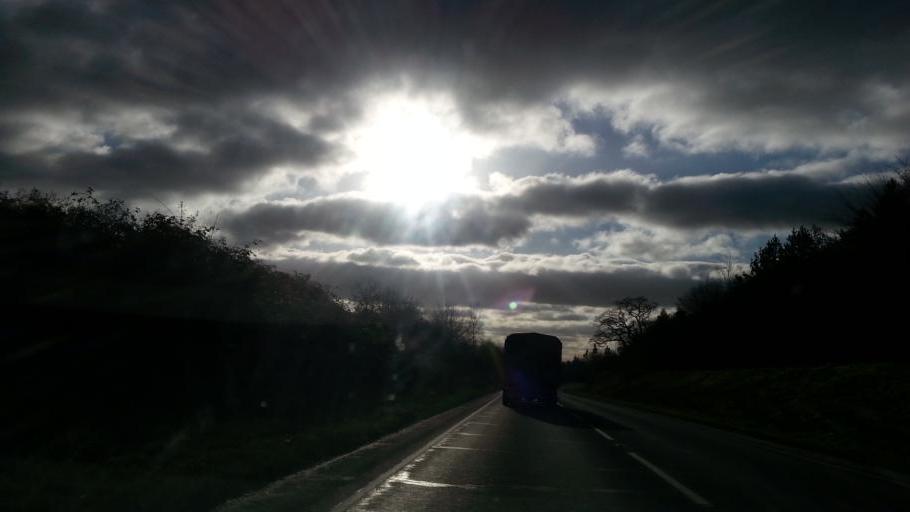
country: GB
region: England
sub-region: Norfolk
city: Harleston
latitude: 52.3703
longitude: 1.2345
